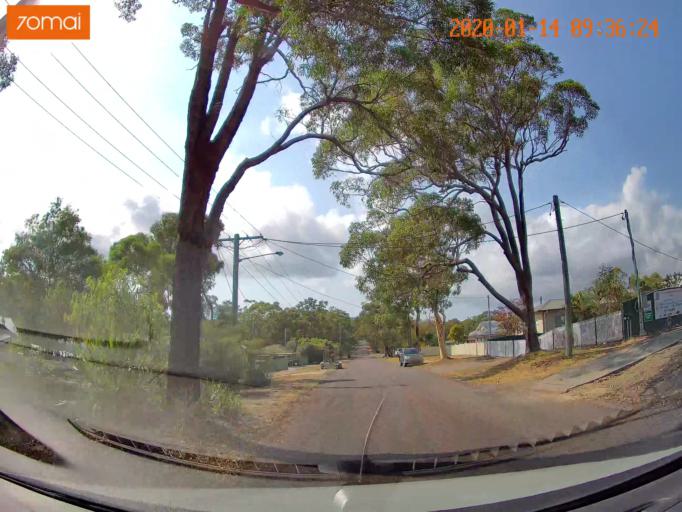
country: AU
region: New South Wales
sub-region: Wyong Shire
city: Kingfisher Shores
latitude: -33.1111
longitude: 151.5563
